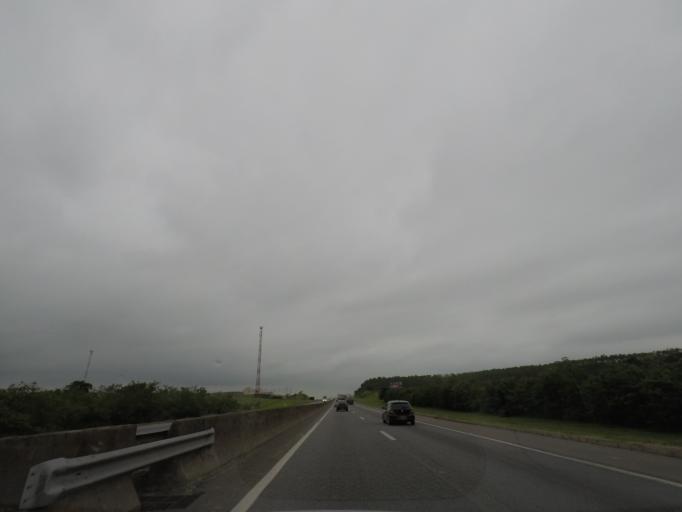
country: BR
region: Sao Paulo
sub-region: Pindamonhangaba
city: Pindamonhangaba
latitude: -22.9496
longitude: -45.3992
